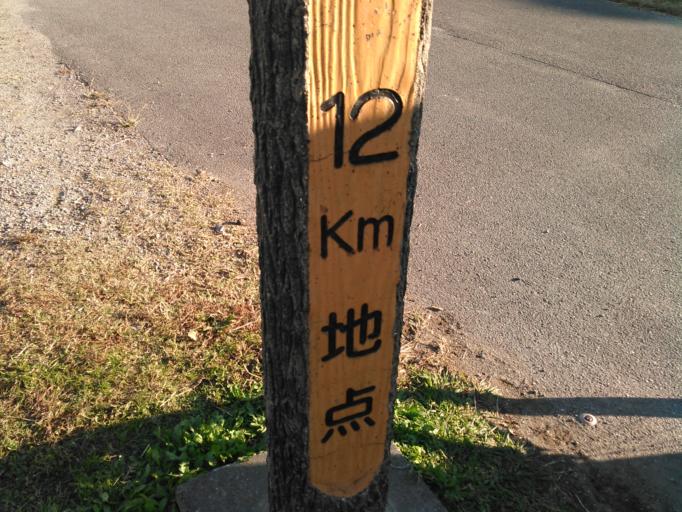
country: JP
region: Tokyo
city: Chofugaoka
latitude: 35.6080
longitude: 139.6240
